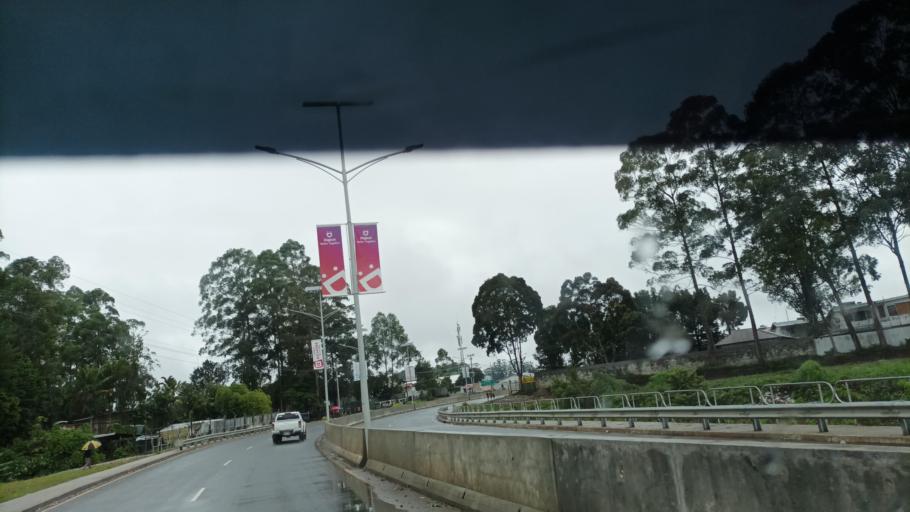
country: PG
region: Western Highlands
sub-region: Hagen
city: Mount Hagen
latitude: -5.8329
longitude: 144.2976
